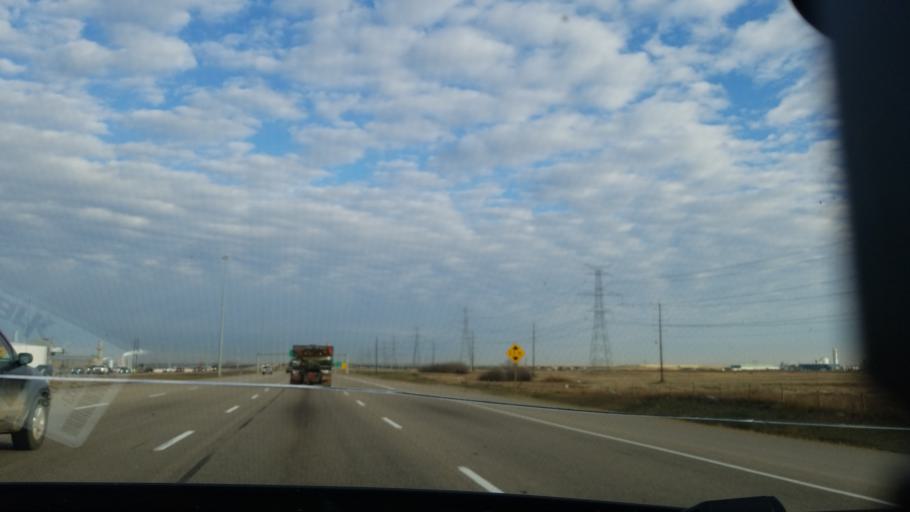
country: CA
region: Alberta
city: Sherwood Park
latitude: 53.5540
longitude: -113.3440
